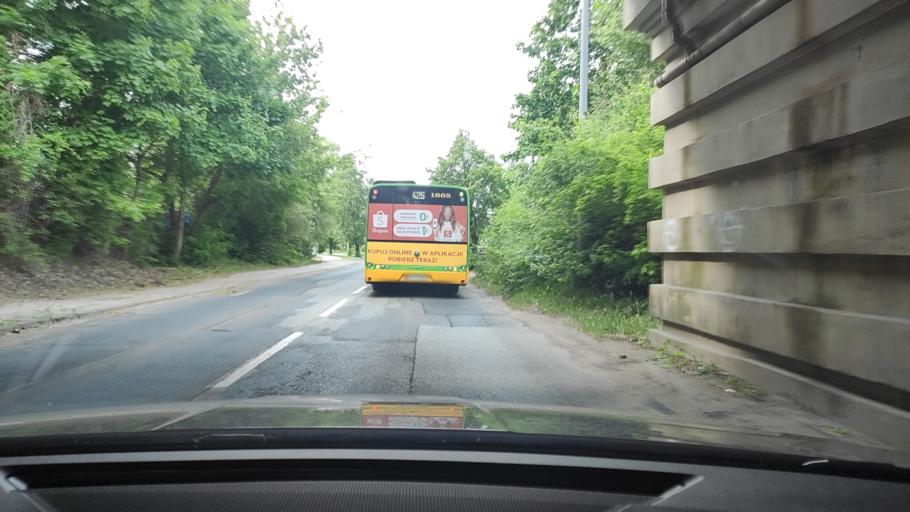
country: PL
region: Greater Poland Voivodeship
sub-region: Powiat poznanski
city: Swarzedz
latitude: 52.3896
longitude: 17.0247
